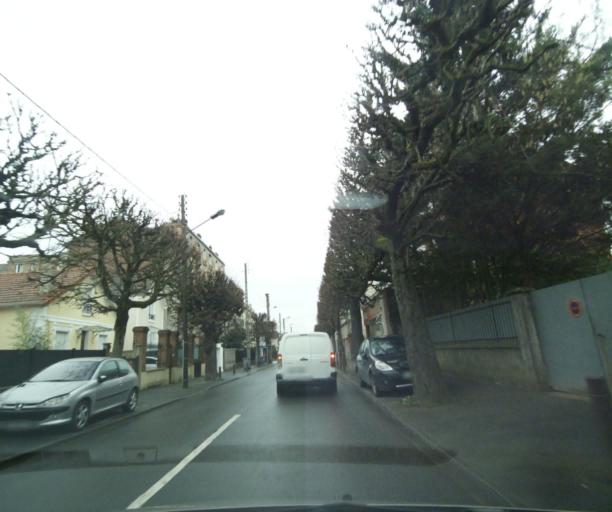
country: FR
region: Ile-de-France
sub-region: Departement du Val-de-Marne
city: Ablon-sur-Seine
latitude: 48.7401
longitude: 2.4235
